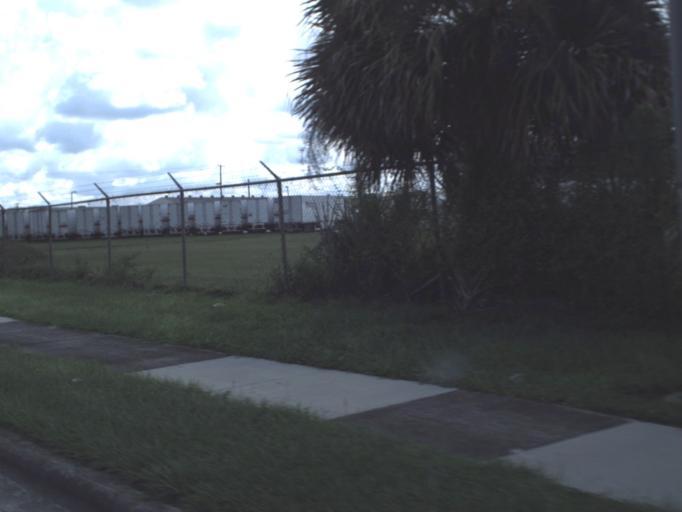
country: US
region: Florida
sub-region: Polk County
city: Auburndale
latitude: 28.0601
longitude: -81.7999
